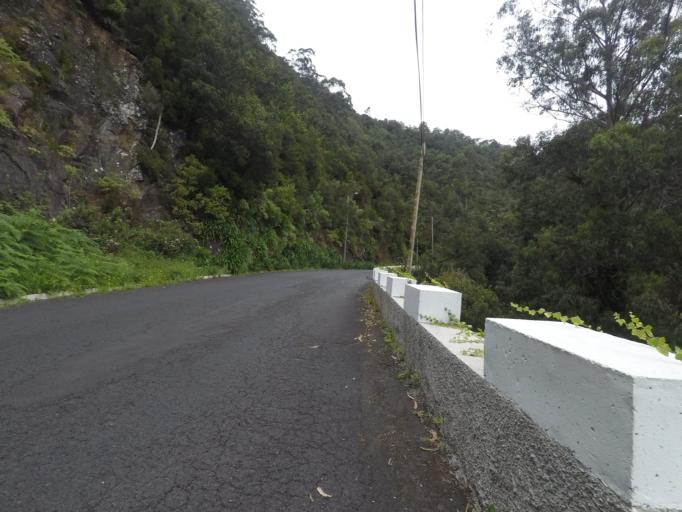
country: PT
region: Madeira
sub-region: Santana
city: Santana
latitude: 32.7906
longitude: -16.8614
